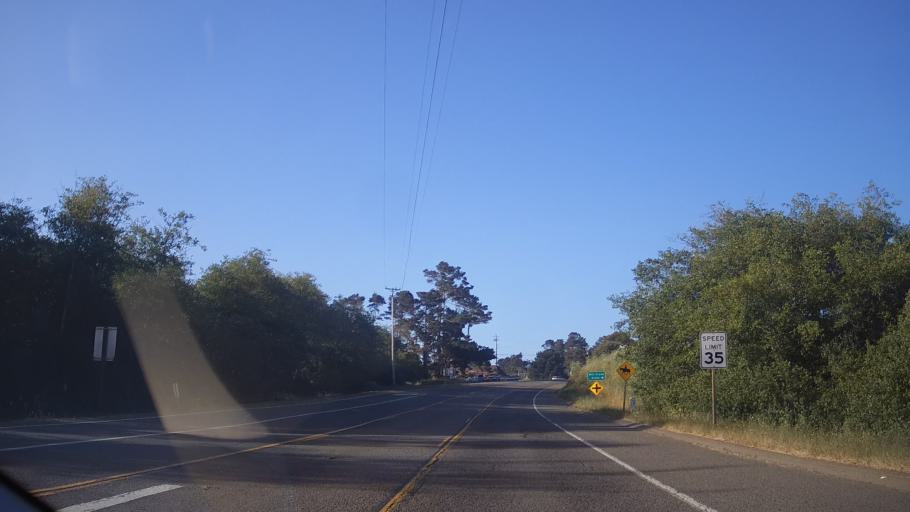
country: US
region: California
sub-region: Mendocino County
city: Fort Bragg
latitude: 39.4883
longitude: -123.7872
